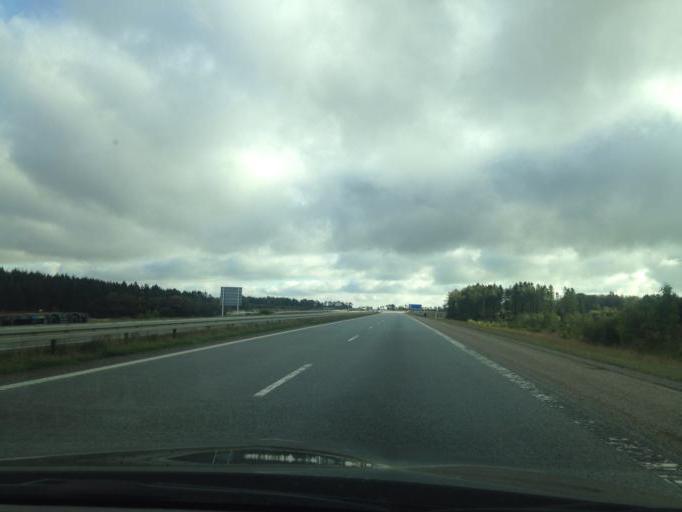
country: DK
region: South Denmark
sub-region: Vejle Kommune
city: Give
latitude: 55.8358
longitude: 9.3007
